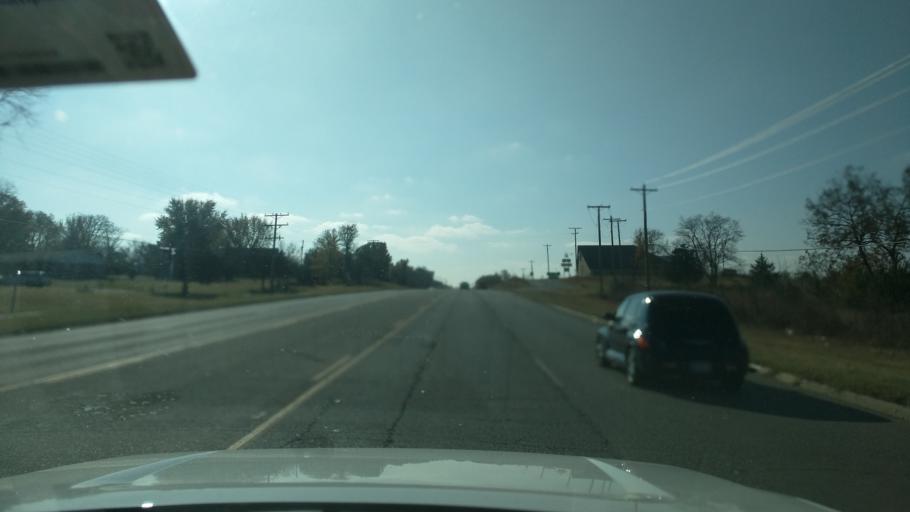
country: US
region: Oklahoma
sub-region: Washington County
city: Bartlesville
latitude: 36.6969
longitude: -95.9352
